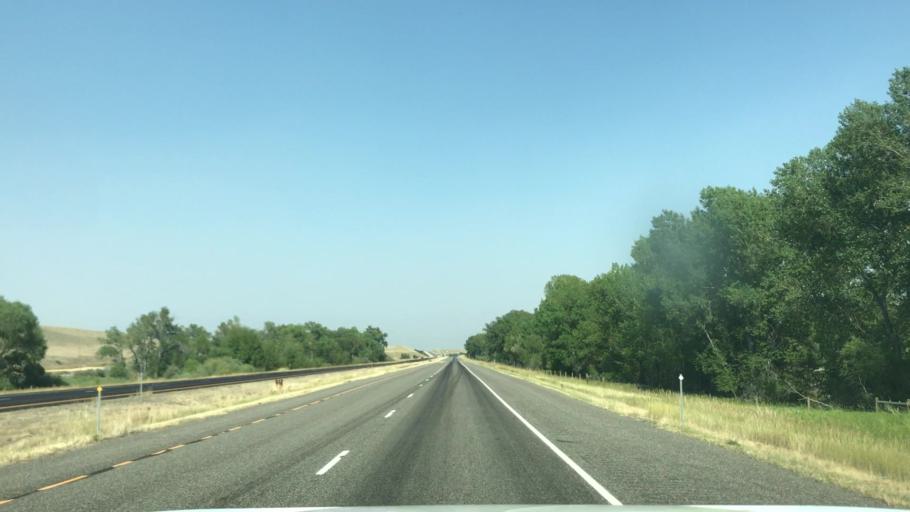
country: US
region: Montana
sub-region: Cascade County
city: Sun Prairie
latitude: 47.2341
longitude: -111.7473
